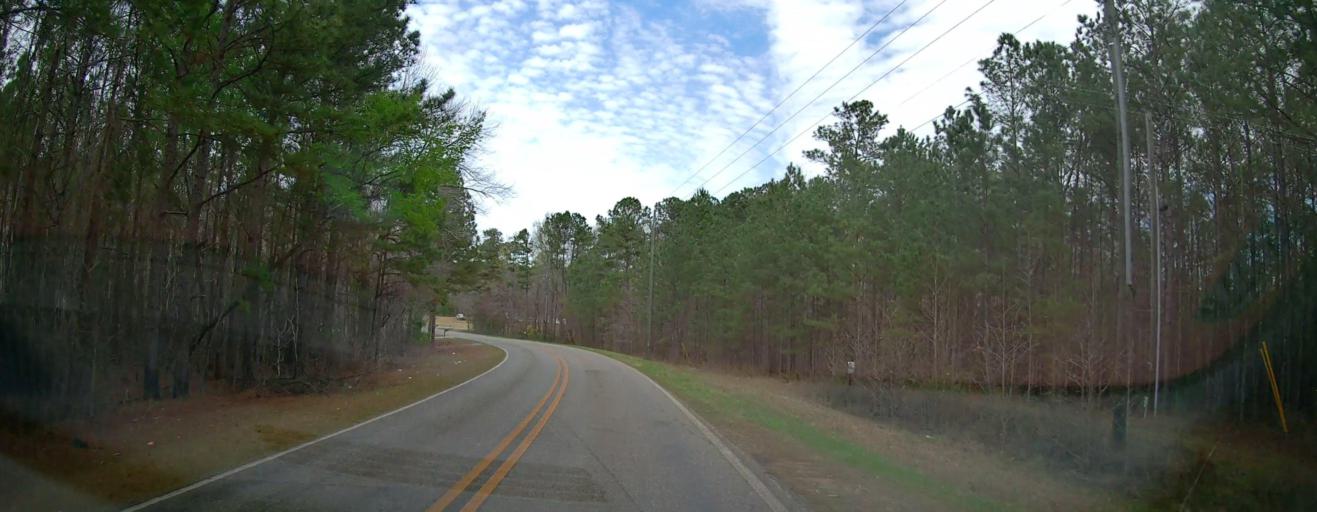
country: US
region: Georgia
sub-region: Bibb County
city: Macon
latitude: 32.9716
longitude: -83.6642
